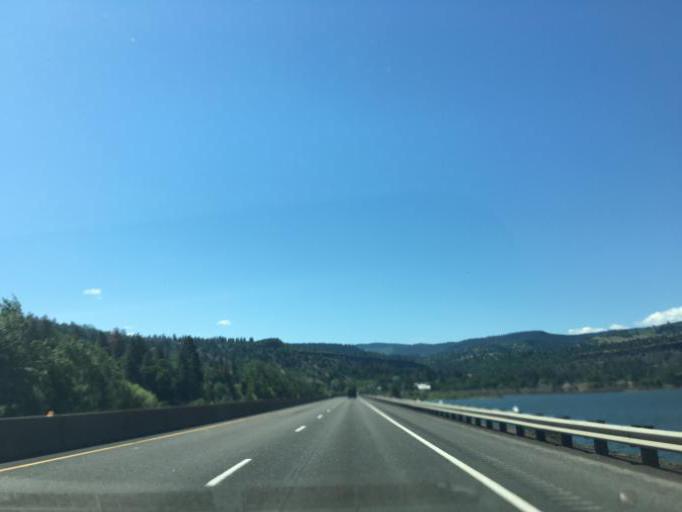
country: US
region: Washington
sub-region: Klickitat County
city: White Salmon
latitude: 45.6902
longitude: -121.3878
